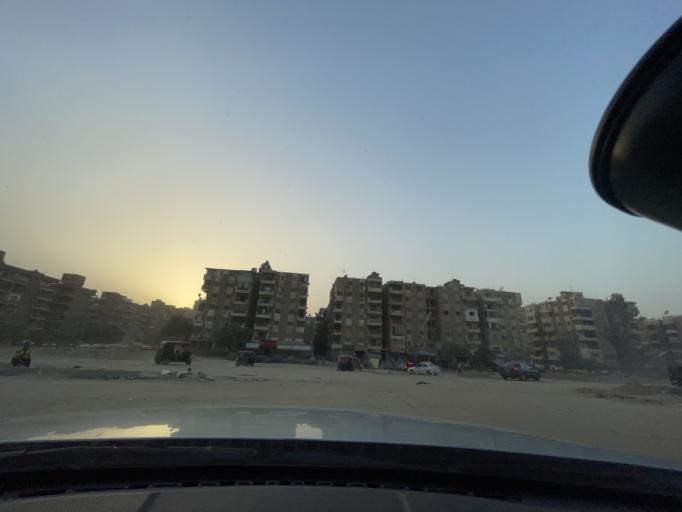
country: EG
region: Muhafazat al Qahirah
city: Cairo
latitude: 30.0608
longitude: 31.3781
